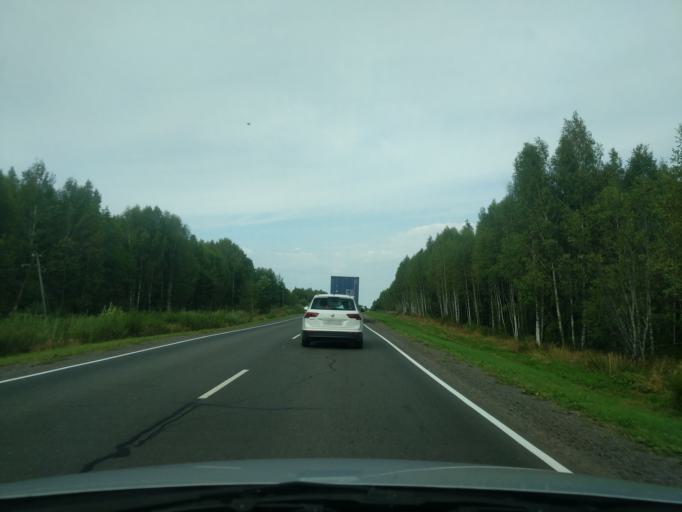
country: RU
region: Kirov
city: Leninskoye
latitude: 58.2847
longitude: 47.2545
